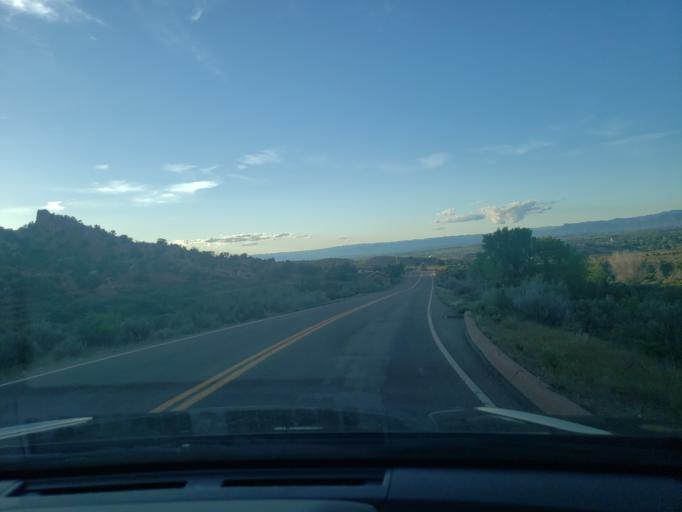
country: US
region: Colorado
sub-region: Mesa County
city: Fruita
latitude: 39.1165
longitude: -108.7304
